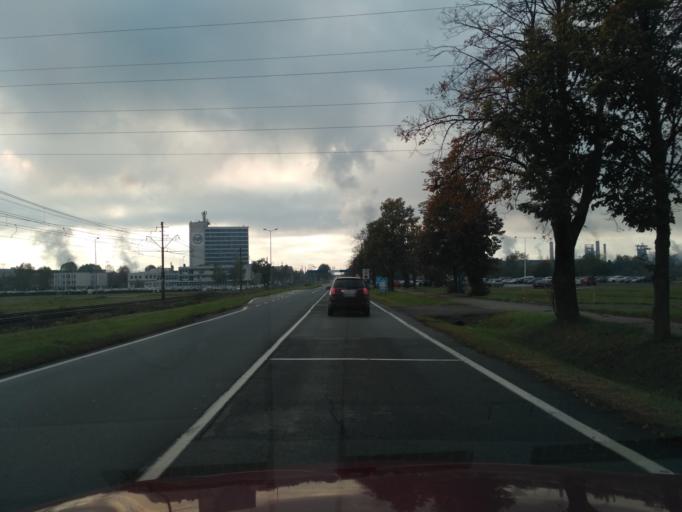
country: SK
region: Kosicky
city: Kosice
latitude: 48.6262
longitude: 21.1867
